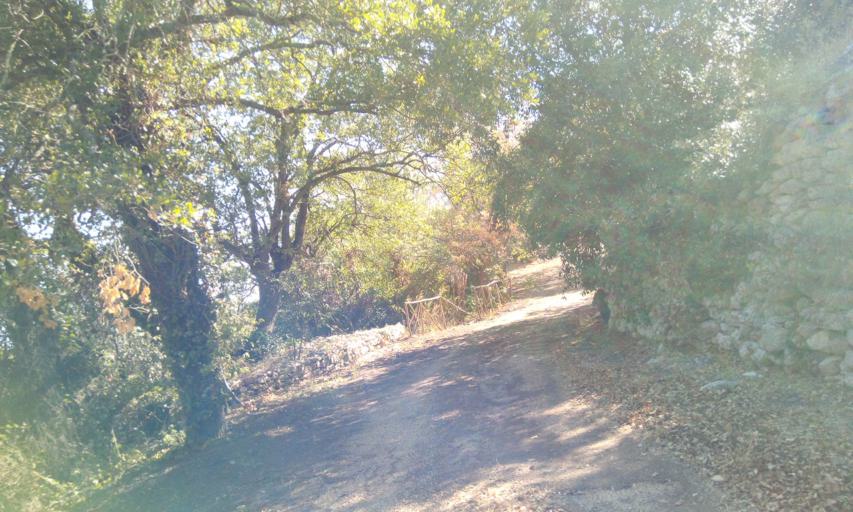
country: IT
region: Apulia
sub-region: Provincia di Bari
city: Gioia del Colle
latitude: 40.8340
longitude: 16.9652
